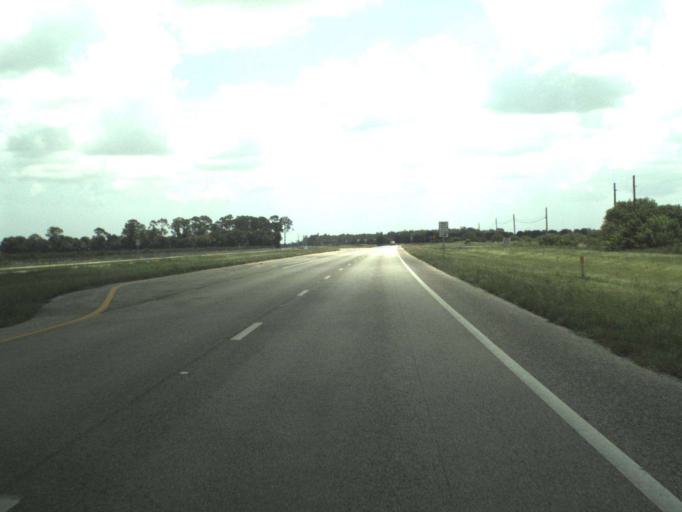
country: US
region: Florida
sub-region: Saint Lucie County
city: Fort Pierce South
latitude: 27.3671
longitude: -80.5388
